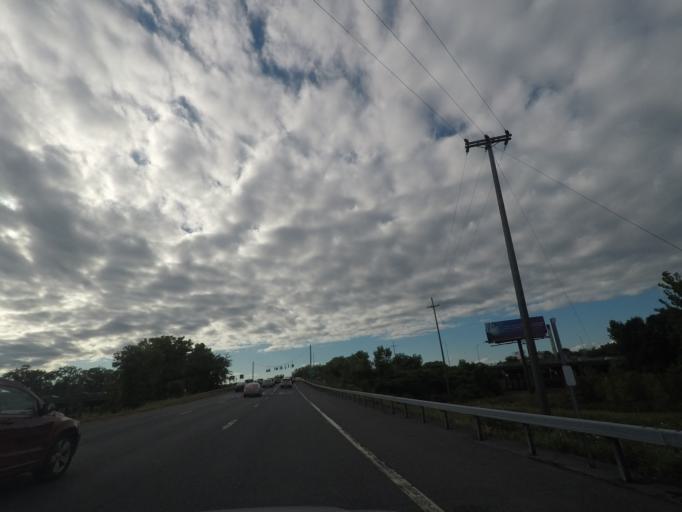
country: US
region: New York
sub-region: Albany County
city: West Albany
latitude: 42.6825
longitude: -73.7832
